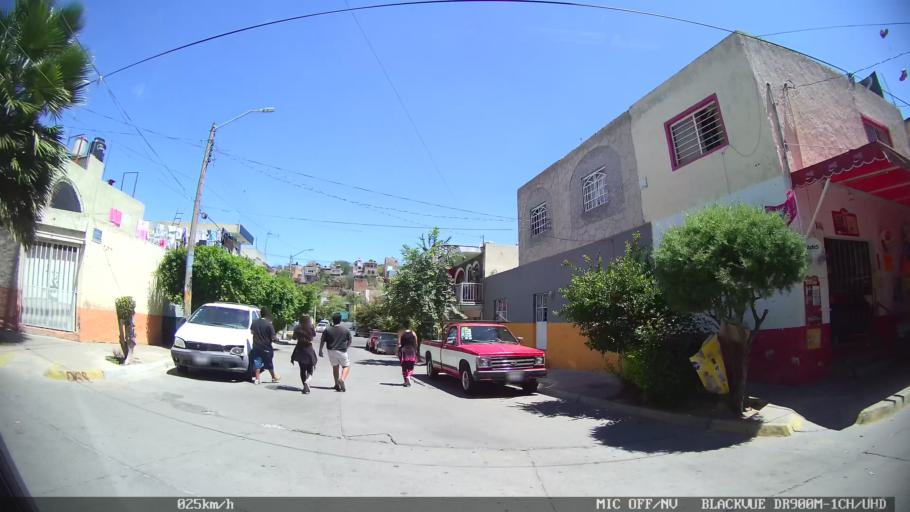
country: MX
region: Jalisco
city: Tlaquepaque
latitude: 20.6859
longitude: -103.2875
